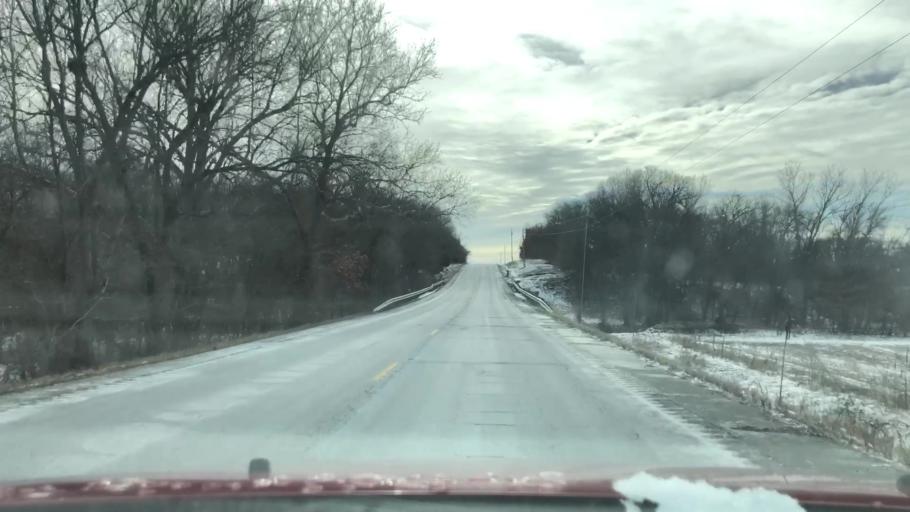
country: US
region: Missouri
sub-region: Jackson County
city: Lone Jack
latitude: 38.9120
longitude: -94.1333
